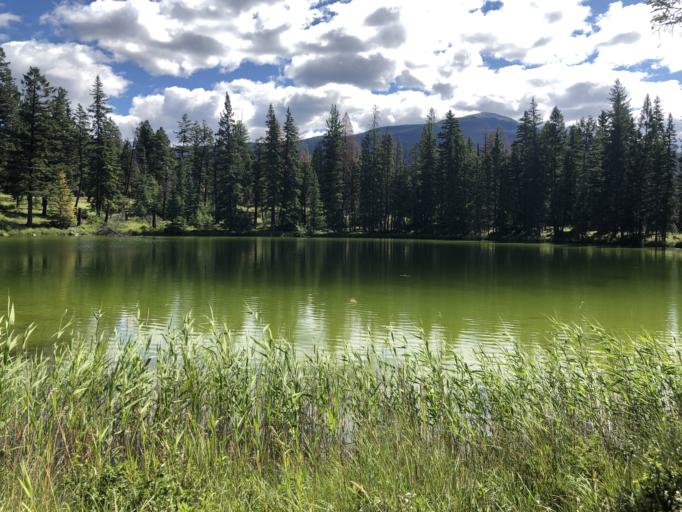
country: CA
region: Alberta
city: Jasper Park Lodge
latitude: 52.8921
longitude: -118.0594
